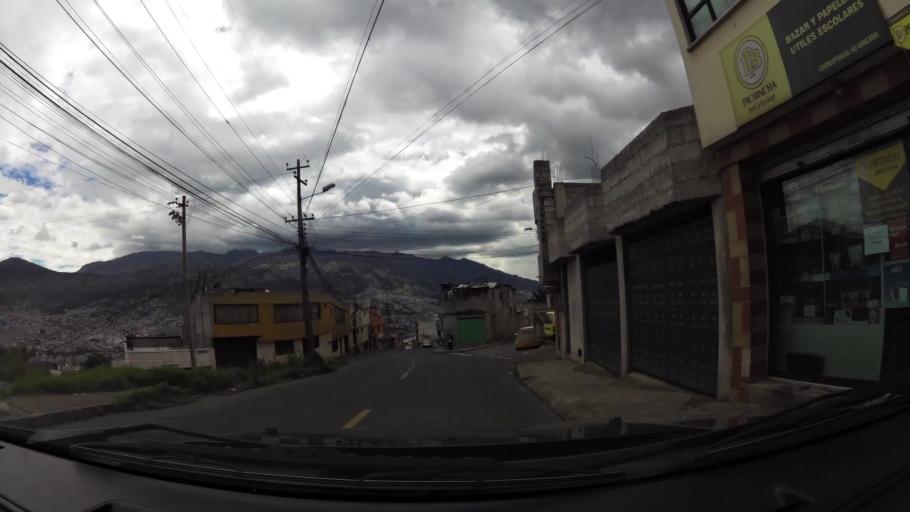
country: EC
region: Pichincha
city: Quito
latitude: -0.2533
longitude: -78.5057
